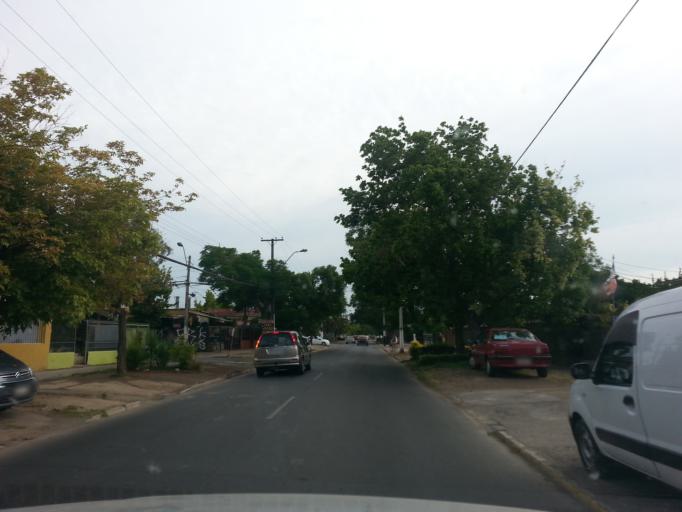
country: CL
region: Santiago Metropolitan
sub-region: Provincia de Santiago
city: Villa Presidente Frei, Nunoa, Santiago, Chile
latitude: -33.4959
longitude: -70.6000
